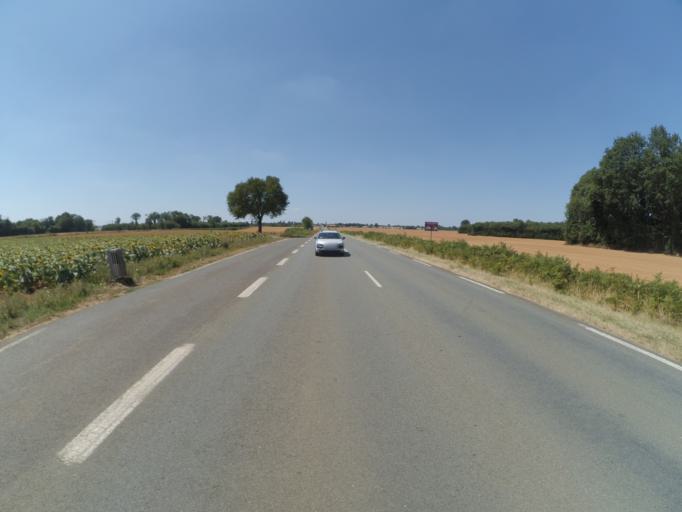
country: FR
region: Poitou-Charentes
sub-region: Departement de la Vienne
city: Rouille
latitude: 46.4228
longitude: 0.0595
